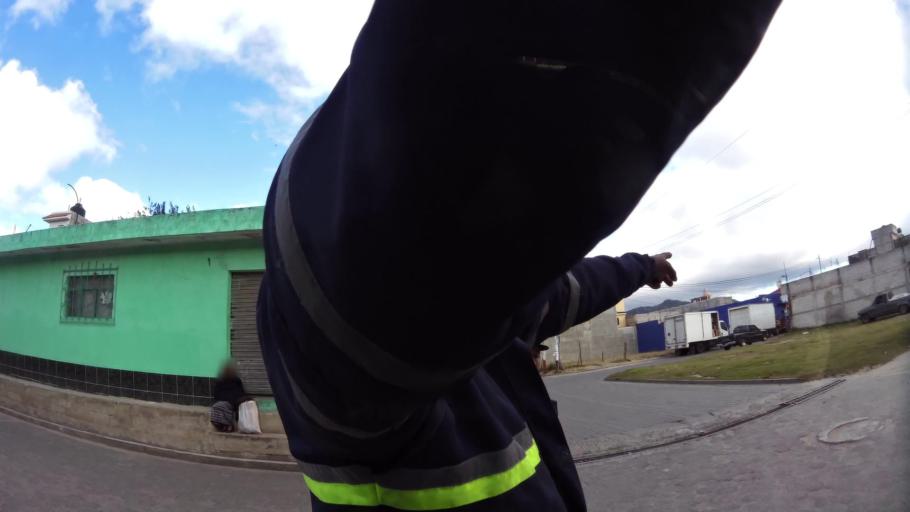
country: GT
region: Quetzaltenango
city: Salcaja
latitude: 14.8763
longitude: -91.4583
